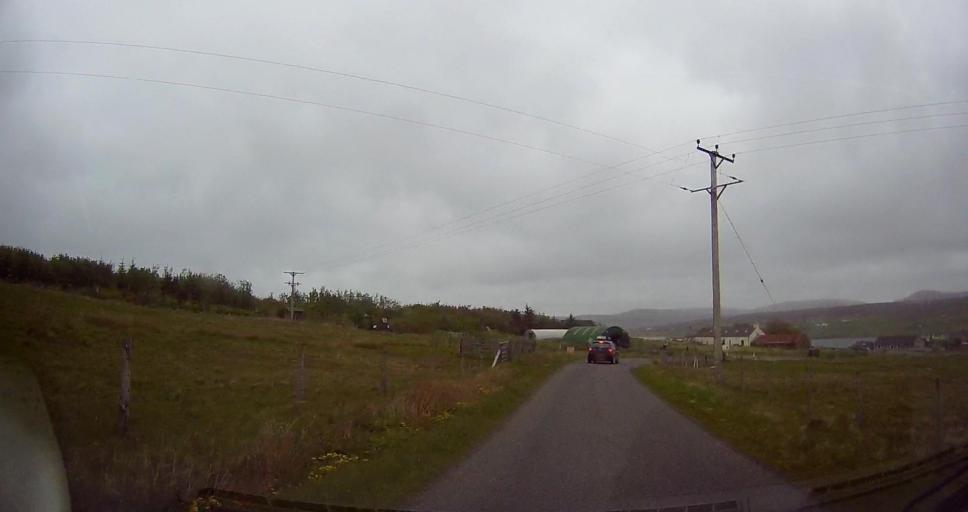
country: GB
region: Scotland
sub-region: Shetland Islands
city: Lerwick
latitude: 60.2846
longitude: -1.3862
